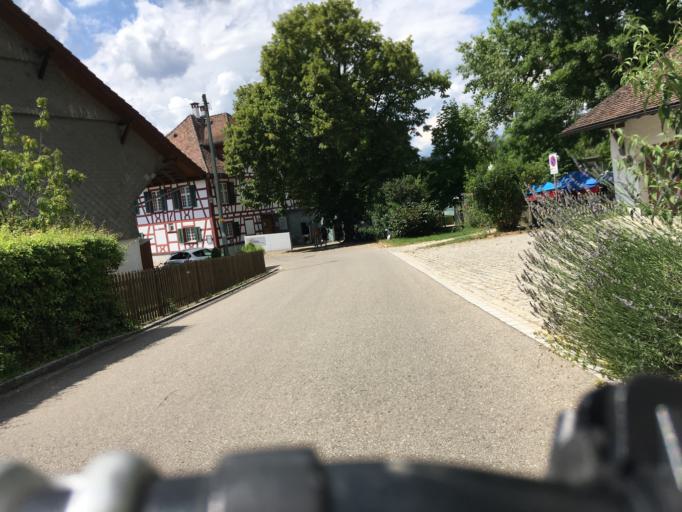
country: DE
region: Baden-Wuerttemberg
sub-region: Freiburg Region
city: Busingen
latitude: 47.6850
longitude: 8.6754
